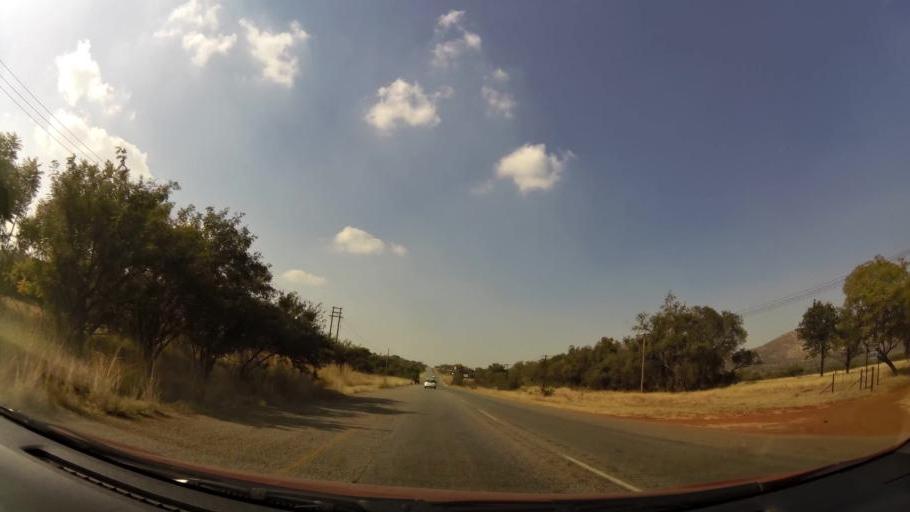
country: ZA
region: North-West
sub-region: Bojanala Platinum District Municipality
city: Rustenburg
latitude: -25.6331
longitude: 27.1708
